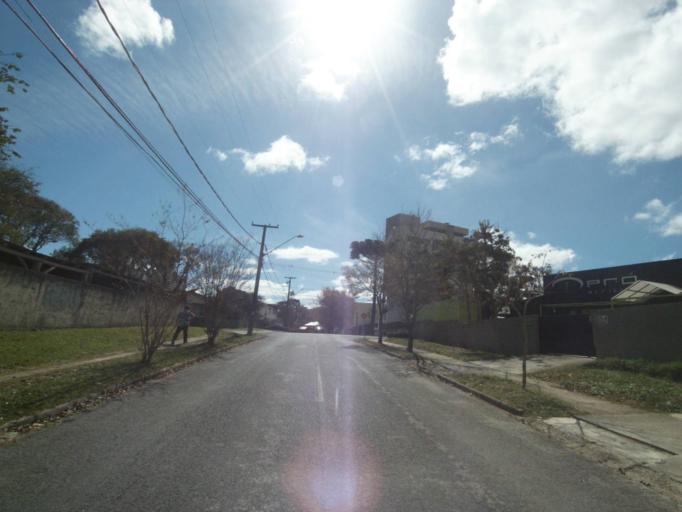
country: BR
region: Parana
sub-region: Curitiba
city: Curitiba
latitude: -25.4697
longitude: -49.2873
